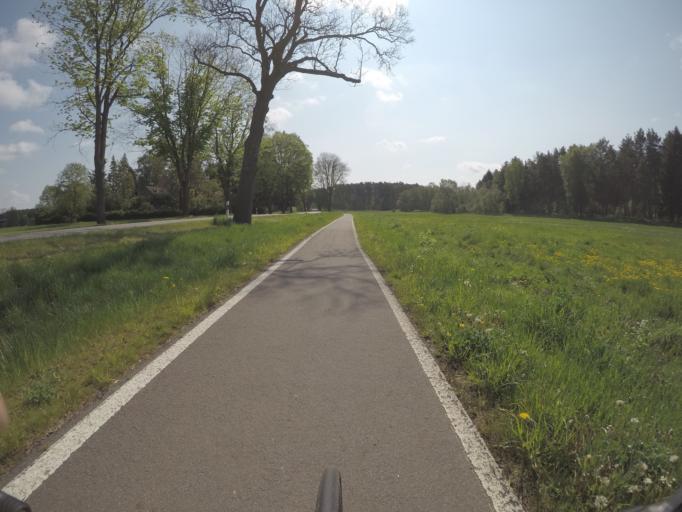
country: DE
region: Brandenburg
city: Wandlitz
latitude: 52.7973
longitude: 13.5122
